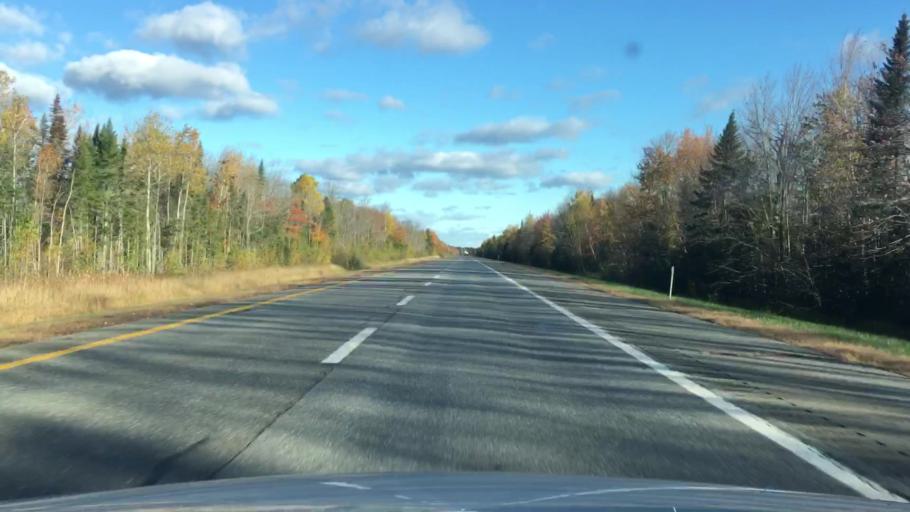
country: US
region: Maine
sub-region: Penobscot County
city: Greenbush
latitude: 45.0817
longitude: -68.6924
